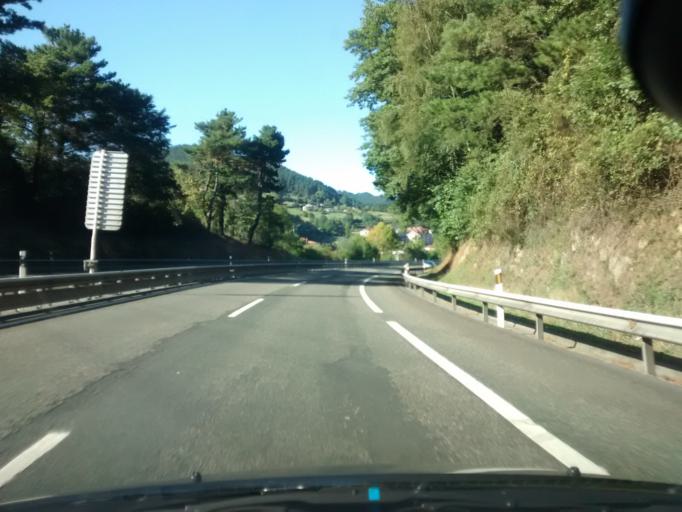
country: ES
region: Basque Country
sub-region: Provincia de Guipuzcoa
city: Elgoibar
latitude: 43.2104
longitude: -2.4162
